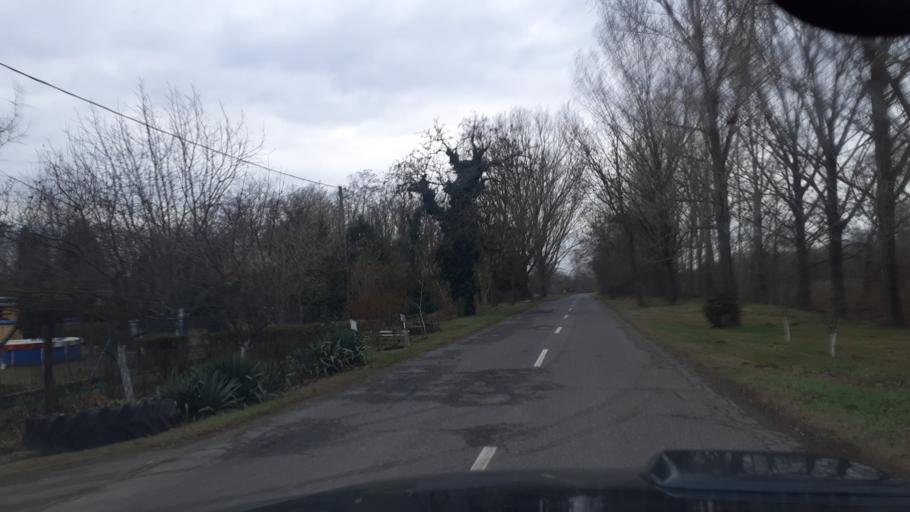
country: HU
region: Bacs-Kiskun
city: Kunszentmiklos
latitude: 46.9267
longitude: 19.1124
